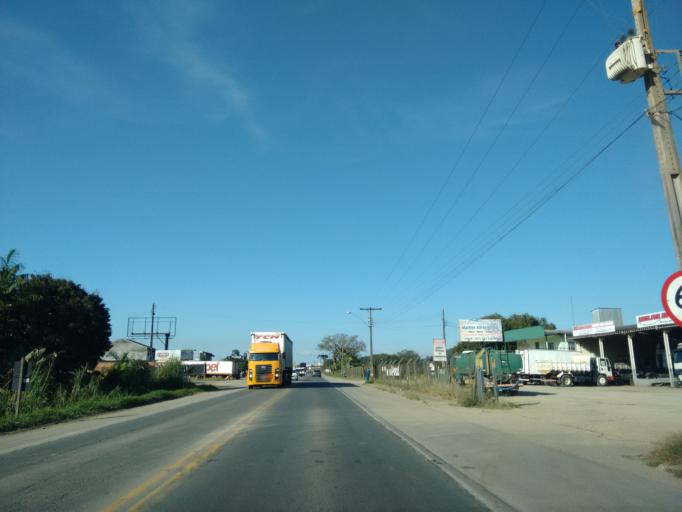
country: BR
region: Santa Catarina
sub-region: Guaramirim
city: Guaramirim
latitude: -26.4754
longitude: -48.9865
